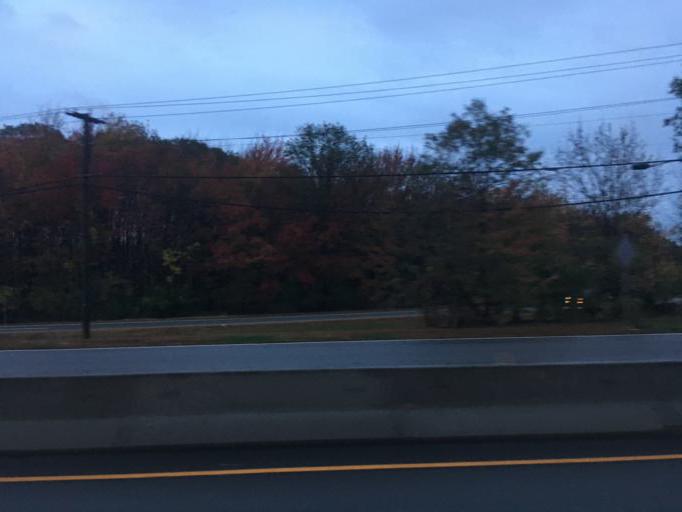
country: US
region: Rhode Island
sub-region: Kent County
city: West Warwick
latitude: 41.6653
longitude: -71.4992
